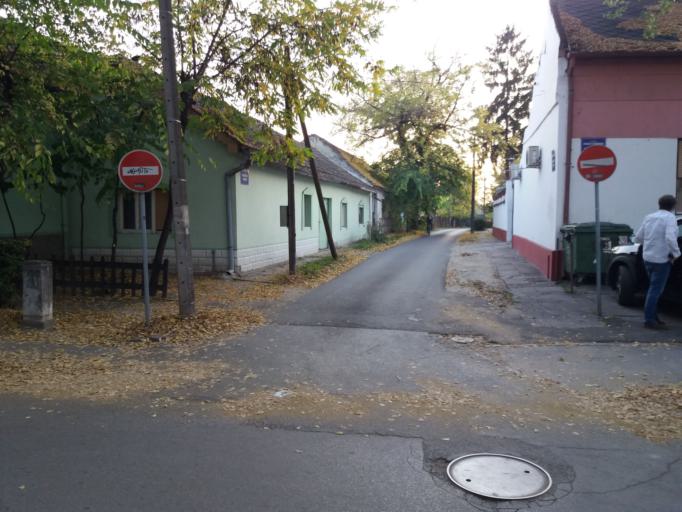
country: RS
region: Autonomna Pokrajina Vojvodina
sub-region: Severnobacki Okrug
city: Subotica
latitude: 46.1069
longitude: 19.6544
